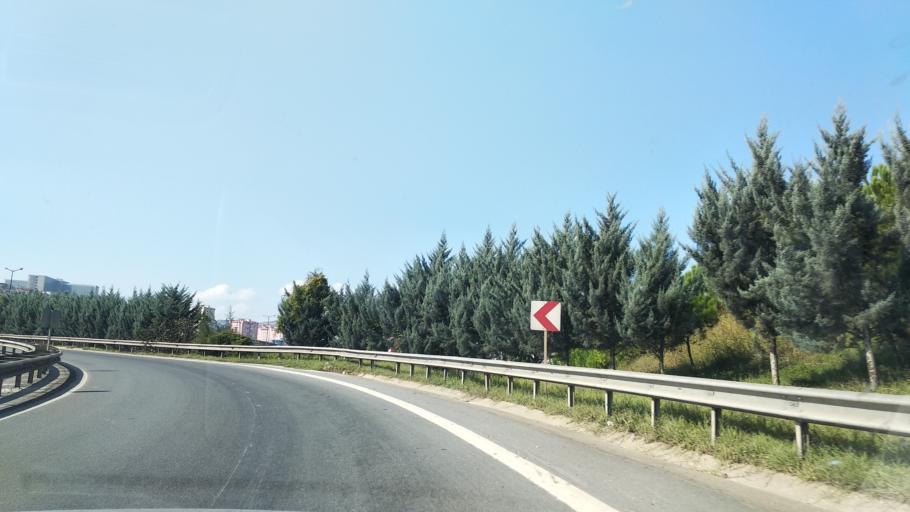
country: TR
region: Kocaeli
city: Kullar
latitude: 40.7830
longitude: 29.9779
